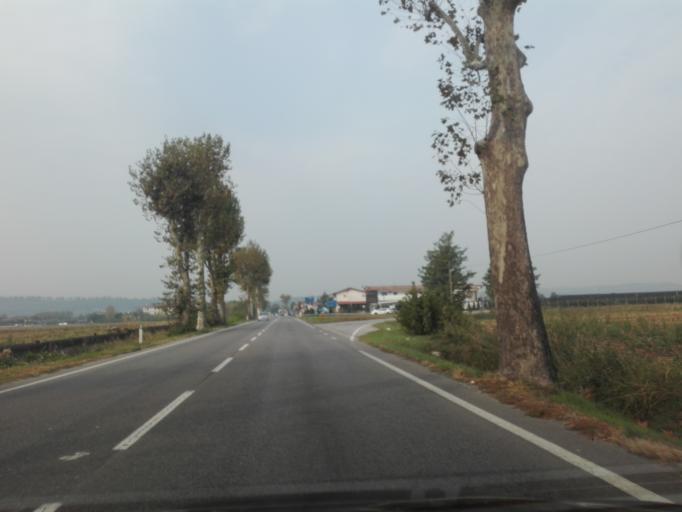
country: IT
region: Veneto
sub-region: Provincia di Verona
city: Sona
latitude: 45.4461
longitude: 10.8573
